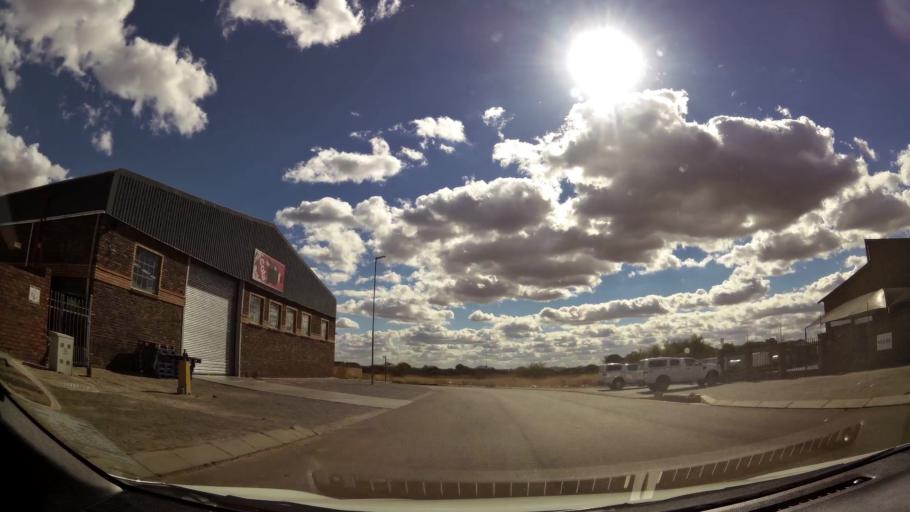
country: ZA
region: Limpopo
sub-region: Capricorn District Municipality
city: Polokwane
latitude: -23.8631
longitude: 29.4785
